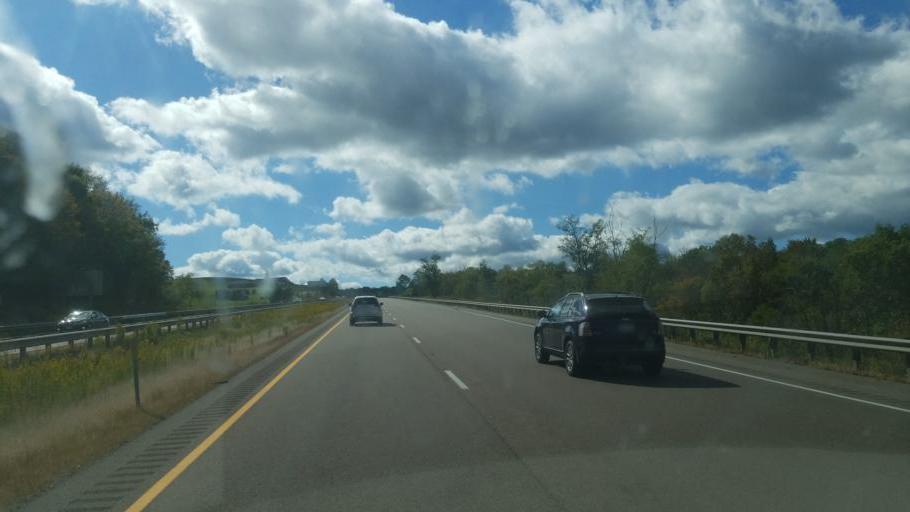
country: US
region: Pennsylvania
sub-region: Somerset County
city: Meyersdale
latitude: 39.6946
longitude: -79.1418
